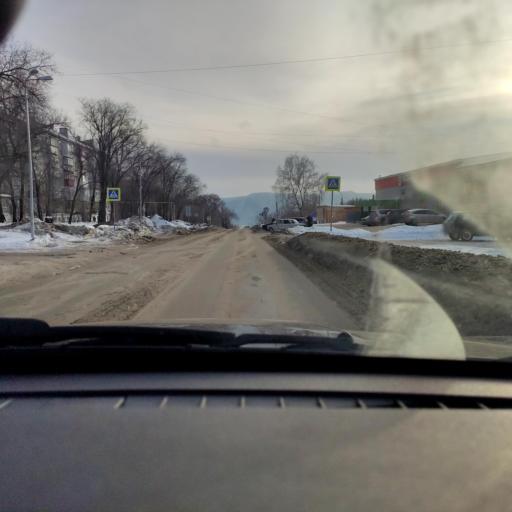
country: RU
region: Samara
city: Pribrezhnyy
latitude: 53.4880
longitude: 49.8468
